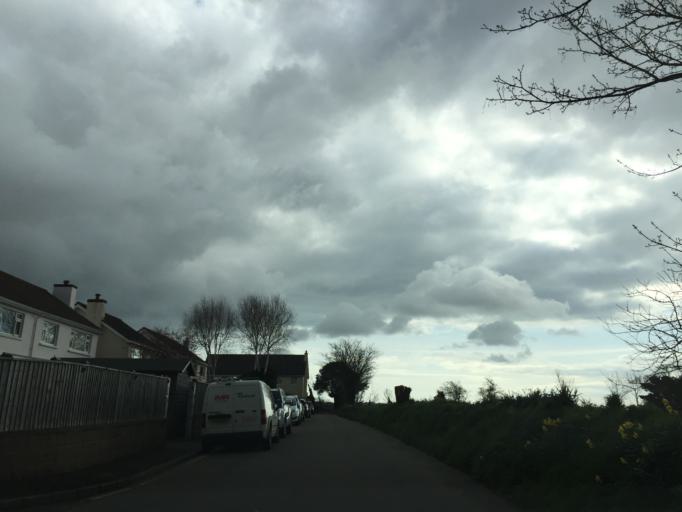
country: JE
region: St Helier
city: Saint Helier
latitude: 49.2085
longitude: -2.1414
